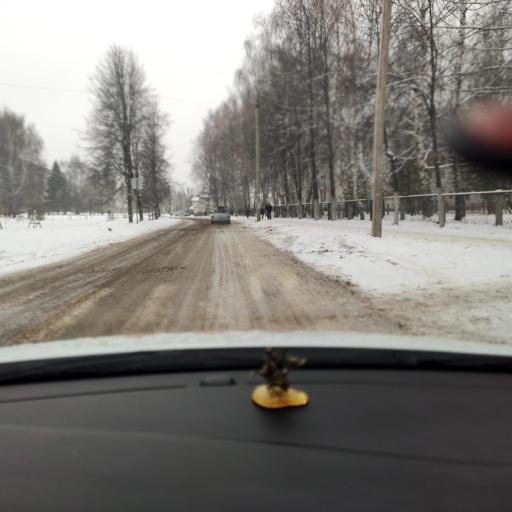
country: RU
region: Tatarstan
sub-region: Zelenodol'skiy Rayon
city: Zelenodolsk
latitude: 55.8517
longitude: 48.5594
